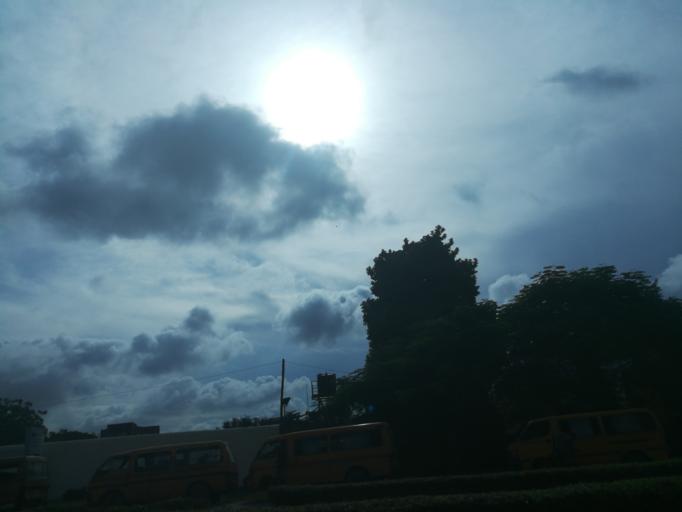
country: NG
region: Lagos
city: Ikeja
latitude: 6.6193
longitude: 3.3579
